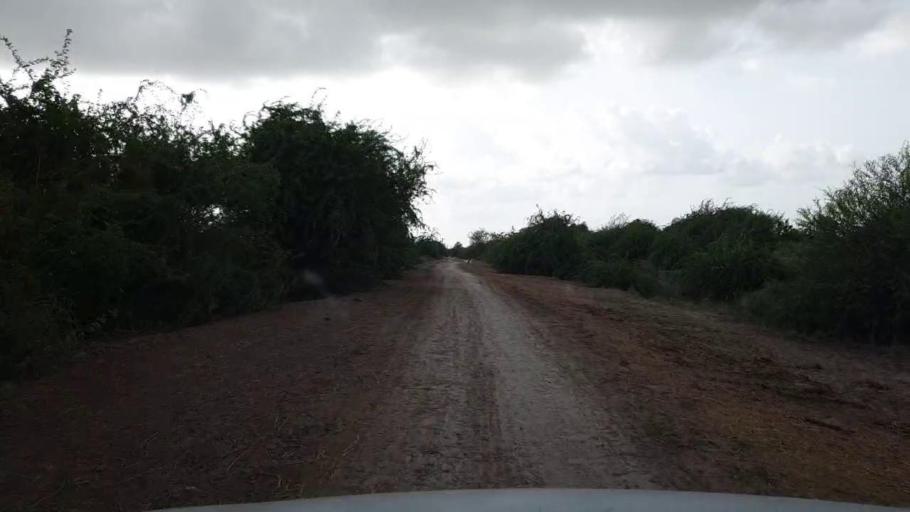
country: PK
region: Sindh
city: Kario
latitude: 24.7521
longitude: 68.6135
